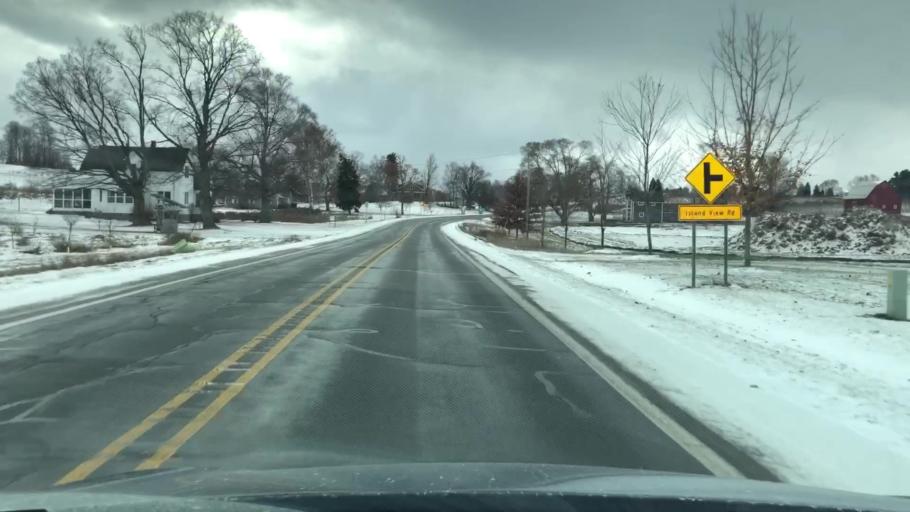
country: US
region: Michigan
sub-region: Antrim County
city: Elk Rapids
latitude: 44.8706
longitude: -85.5153
